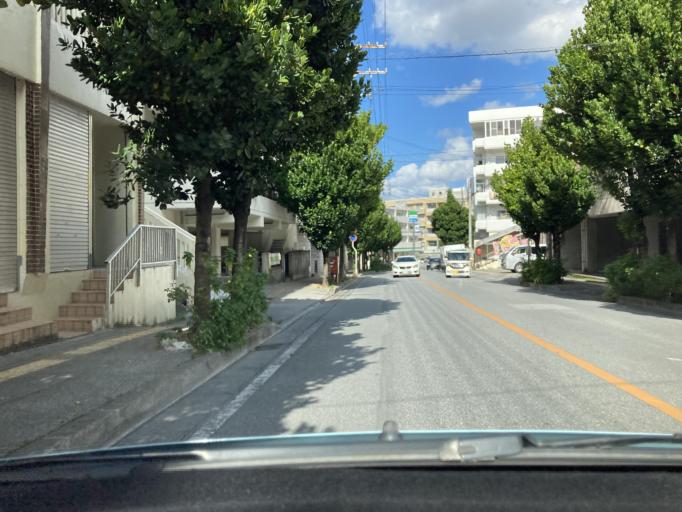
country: JP
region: Okinawa
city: Naha-shi
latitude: 26.2130
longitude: 127.6995
